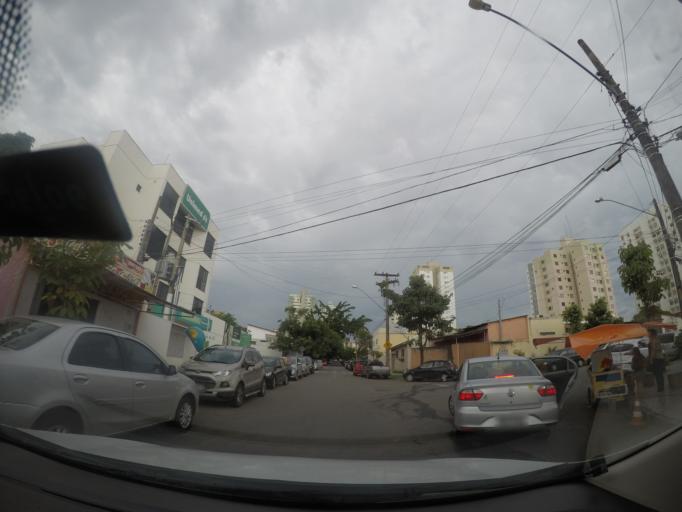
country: BR
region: Goias
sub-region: Goiania
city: Goiania
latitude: -16.6675
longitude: -49.2668
